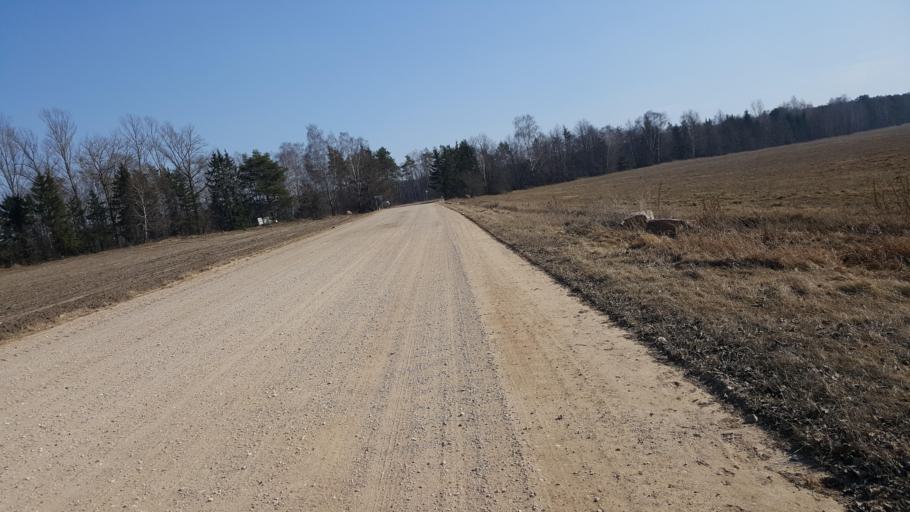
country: BY
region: Brest
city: Kamyanyets
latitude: 52.3555
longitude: 23.7736
